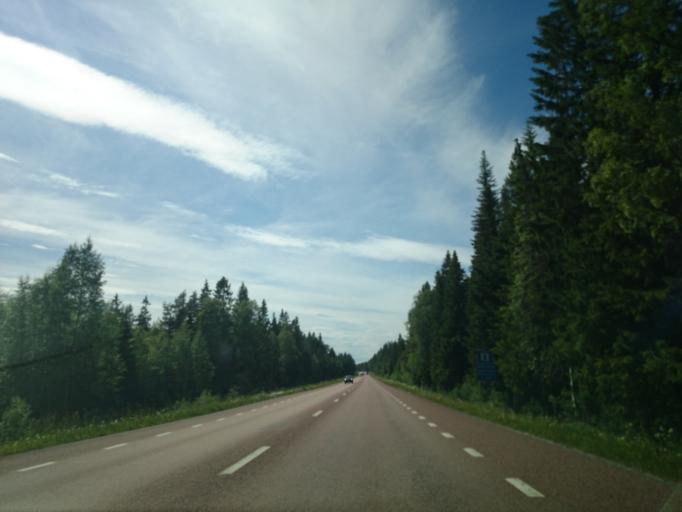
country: SE
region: Jaemtland
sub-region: Krokoms Kommun
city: Krokom
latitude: 63.3260
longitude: 14.3256
